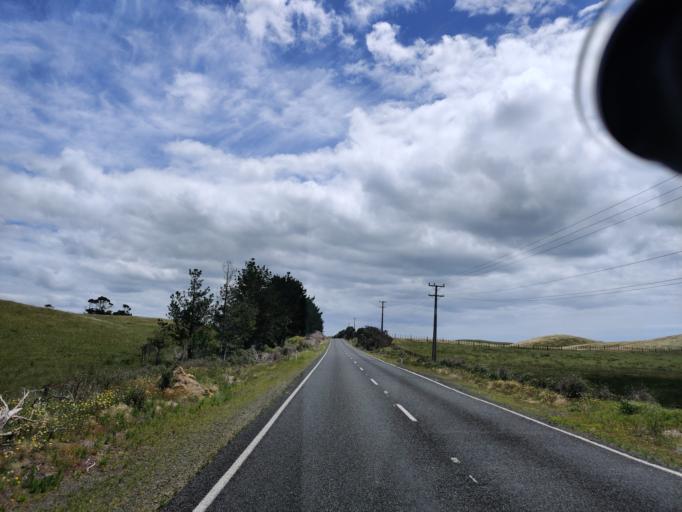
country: NZ
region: Northland
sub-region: Far North District
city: Kaitaia
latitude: -34.7224
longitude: 173.0419
